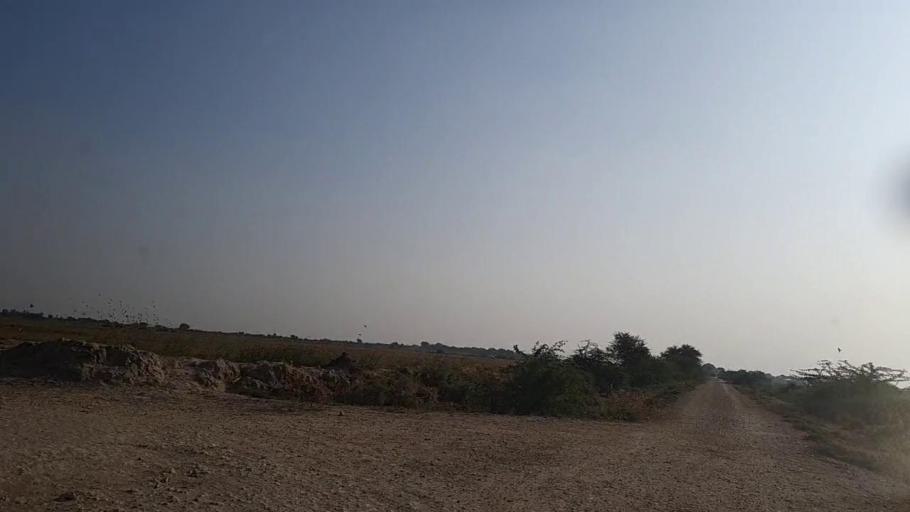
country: PK
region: Sindh
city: Jati
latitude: 24.4602
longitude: 68.2914
